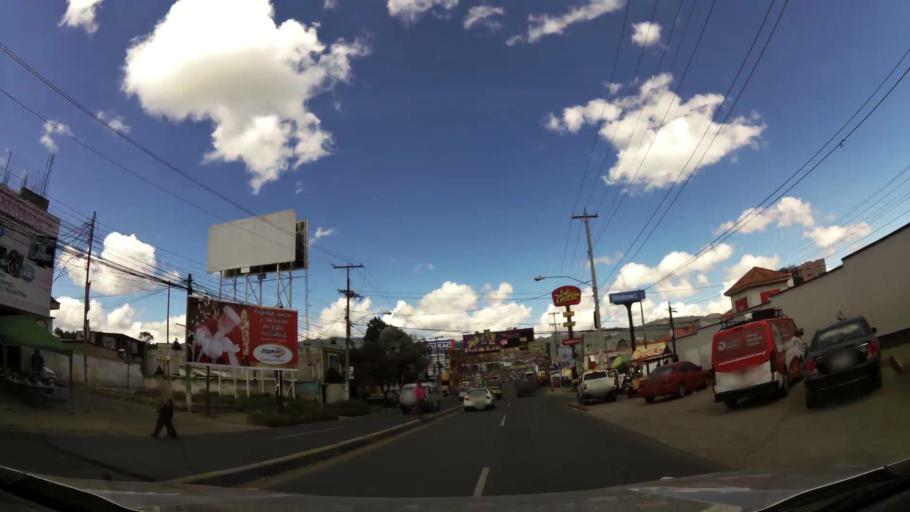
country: GT
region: Quetzaltenango
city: Quetzaltenango
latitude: 14.8491
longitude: -91.5367
